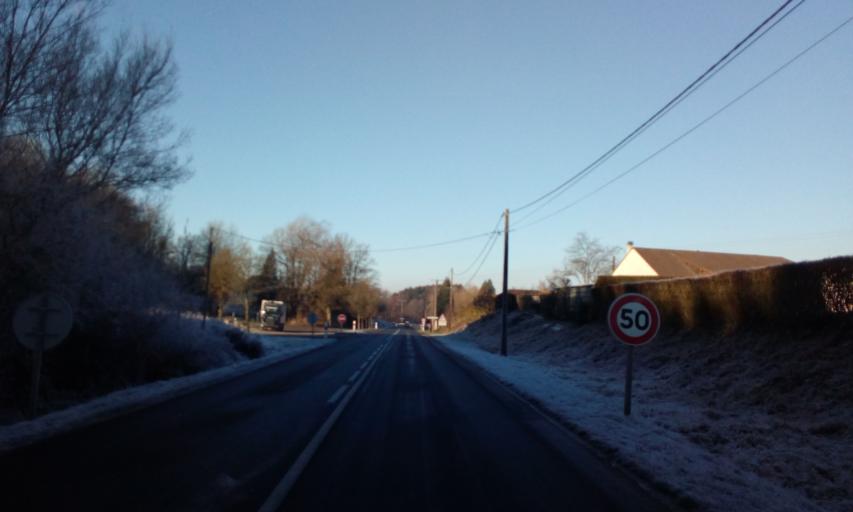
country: FR
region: Champagne-Ardenne
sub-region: Departement des Ardennes
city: Rimogne
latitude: 49.8280
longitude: 4.5026
